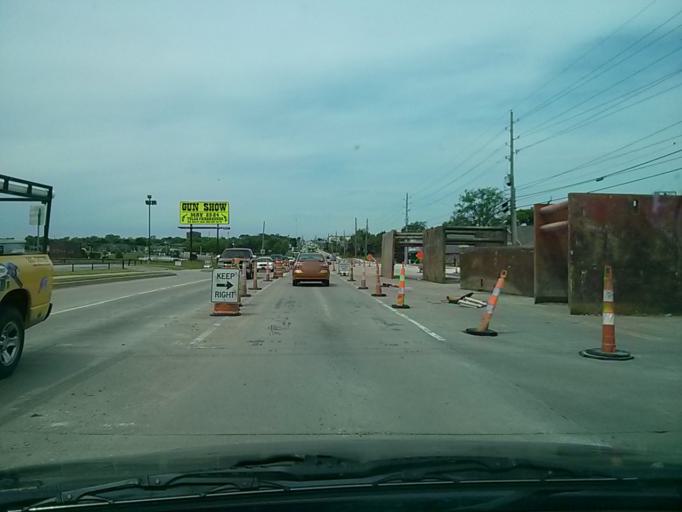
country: US
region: Oklahoma
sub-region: Tulsa County
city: Broken Arrow
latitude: 36.0754
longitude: -95.8686
